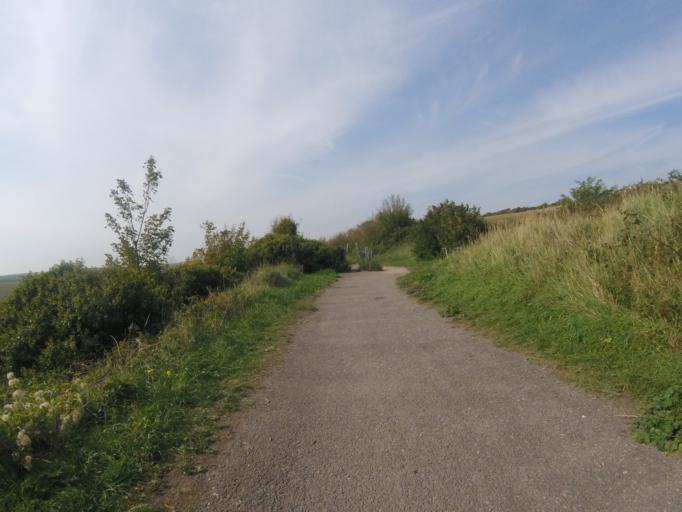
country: GB
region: England
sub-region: East Sussex
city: Portslade
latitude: 50.8578
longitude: -0.1985
